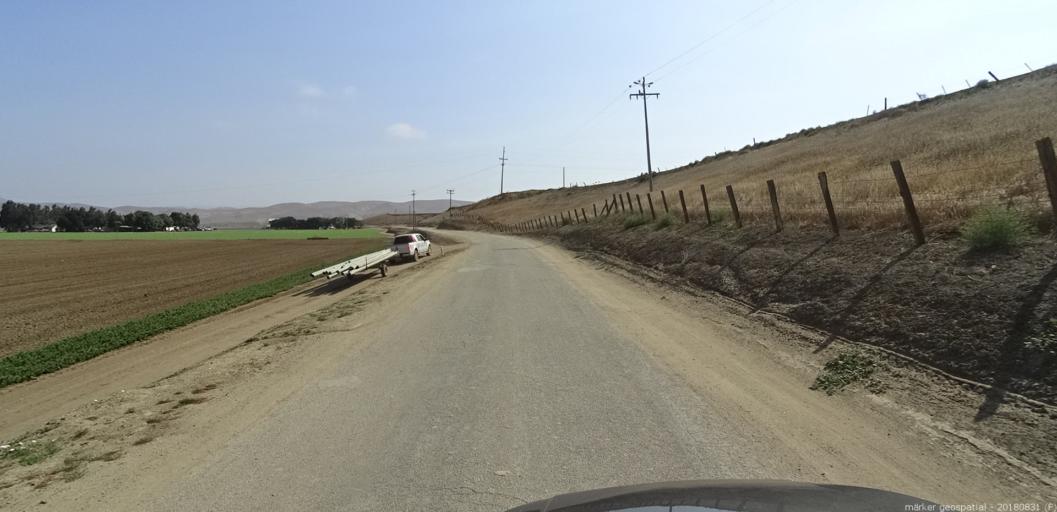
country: US
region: California
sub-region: Monterey County
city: Greenfield
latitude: 36.3052
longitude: -121.2052
